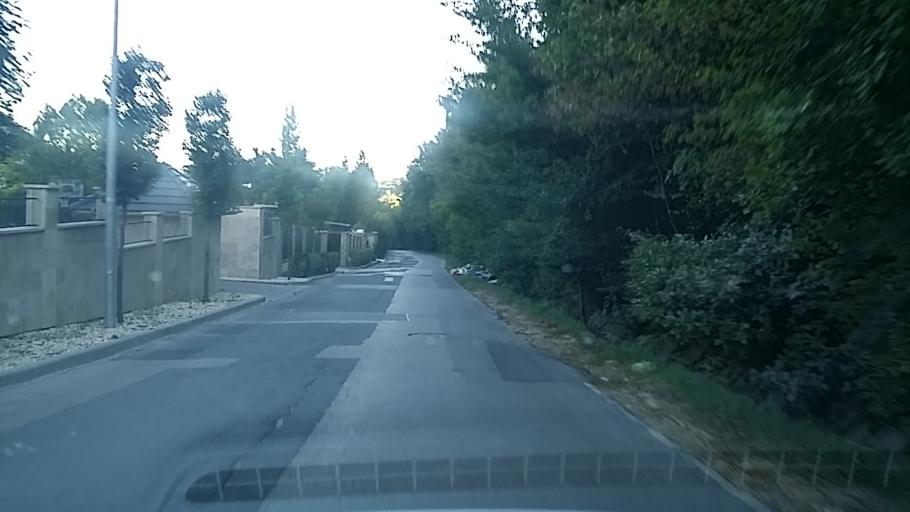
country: HU
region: Budapest
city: Budapest II. keruelet
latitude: 47.5426
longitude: 18.9973
